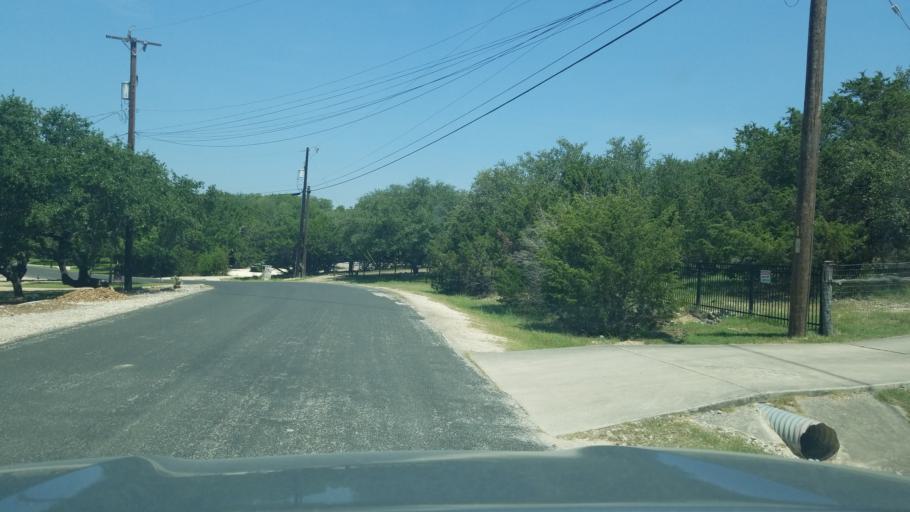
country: US
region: Texas
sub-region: Bexar County
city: Timberwood Park
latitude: 29.6925
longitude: -98.4867
